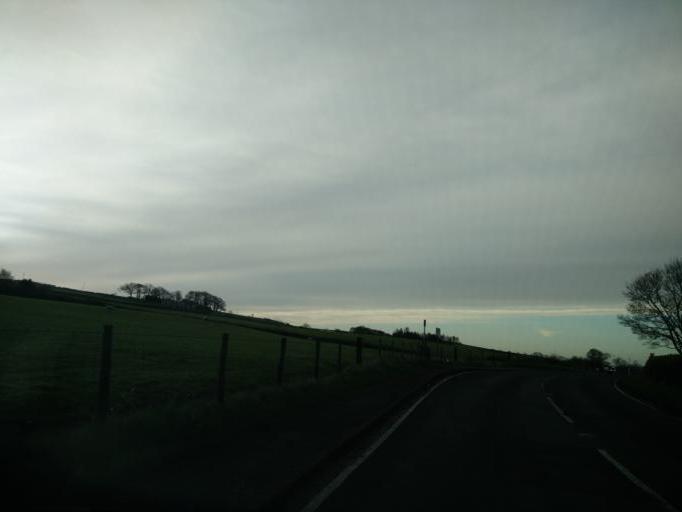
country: GB
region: England
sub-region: County Durham
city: Crook
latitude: 54.6882
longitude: -1.7402
